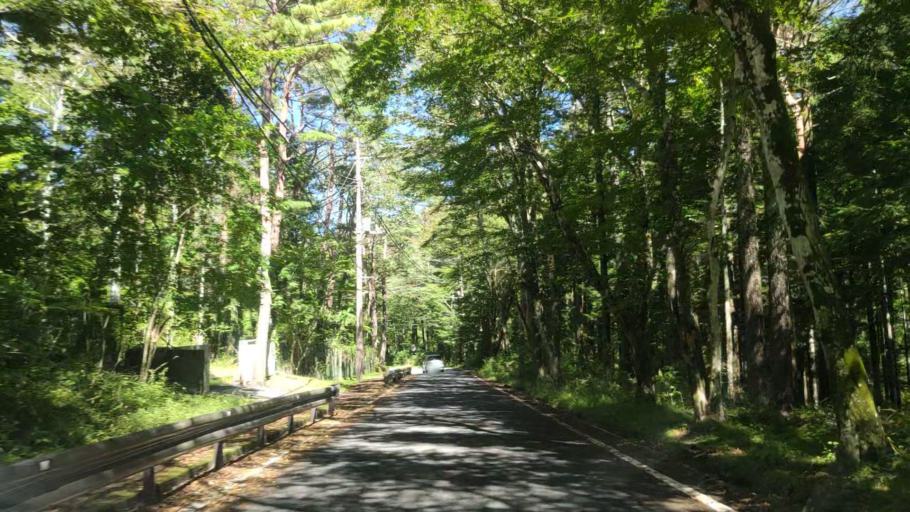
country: JP
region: Shizuoka
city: Gotemba
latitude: 35.4063
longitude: 138.8576
